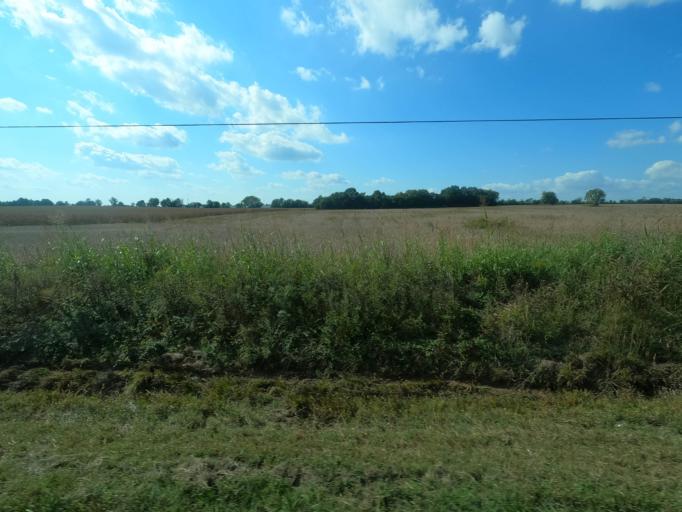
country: US
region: Illinois
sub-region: Massac County
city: Metropolis
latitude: 37.1800
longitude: -88.6767
